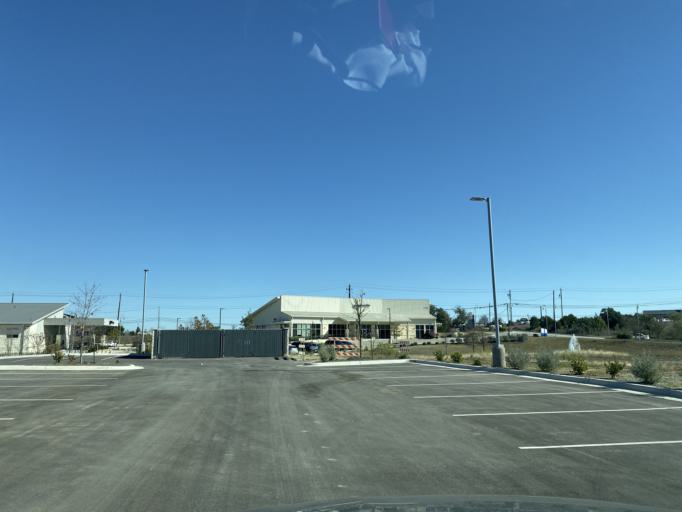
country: US
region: Texas
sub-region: Travis County
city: The Hills
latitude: 30.3325
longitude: -97.9699
